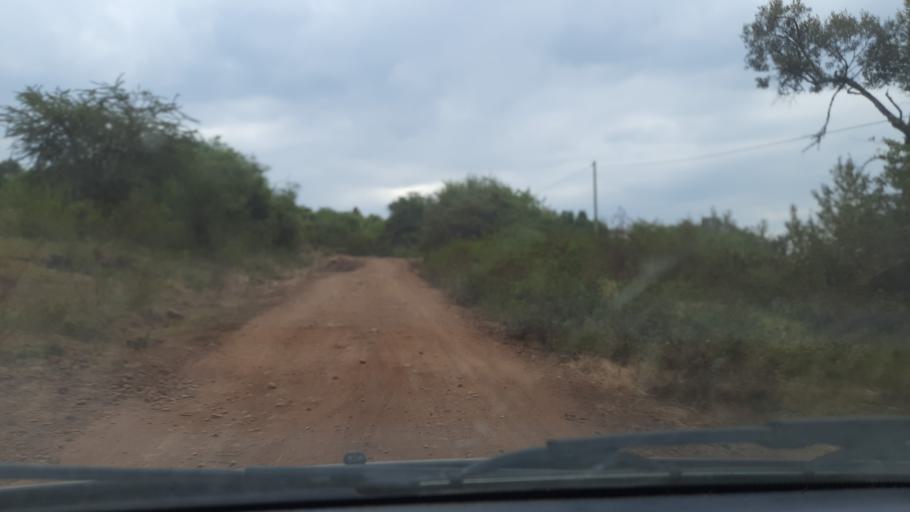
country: TZ
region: Kilimanjaro
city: Moshi
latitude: -2.8593
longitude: 37.2618
